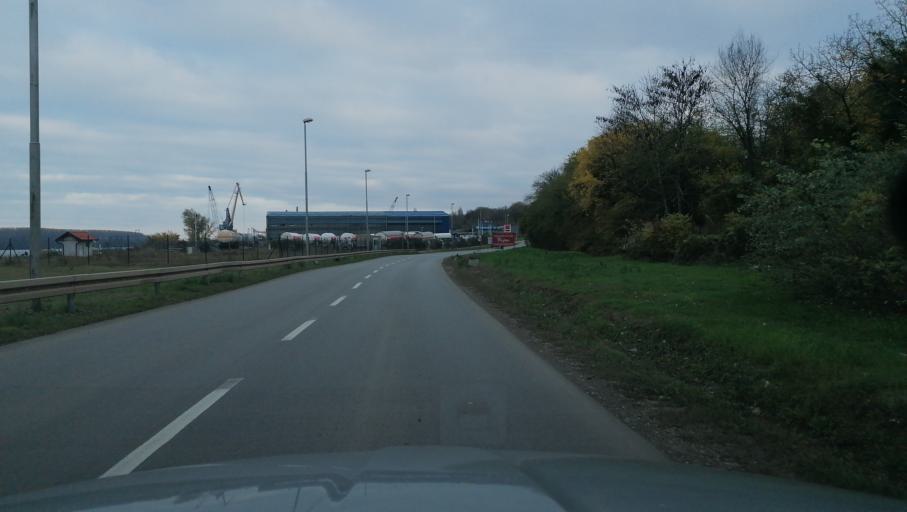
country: RS
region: Central Serbia
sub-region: Podunavski Okrug
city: Smederevo
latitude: 44.6602
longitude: 20.8903
